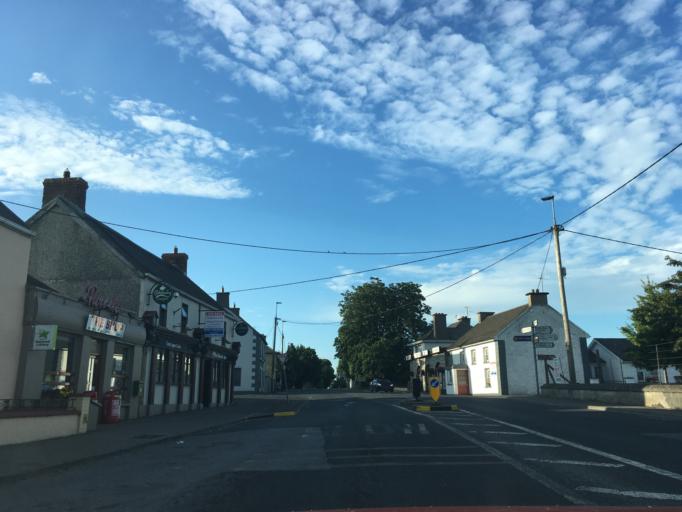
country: IE
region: Munster
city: Cahir
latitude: 52.4403
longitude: -7.8824
